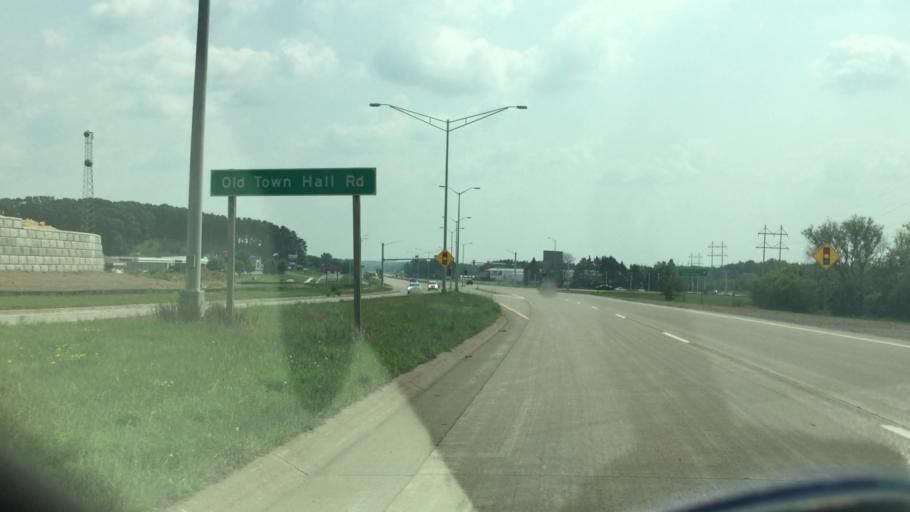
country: US
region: Wisconsin
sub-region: Eau Claire County
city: Altoona
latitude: 44.7635
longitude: -91.4590
